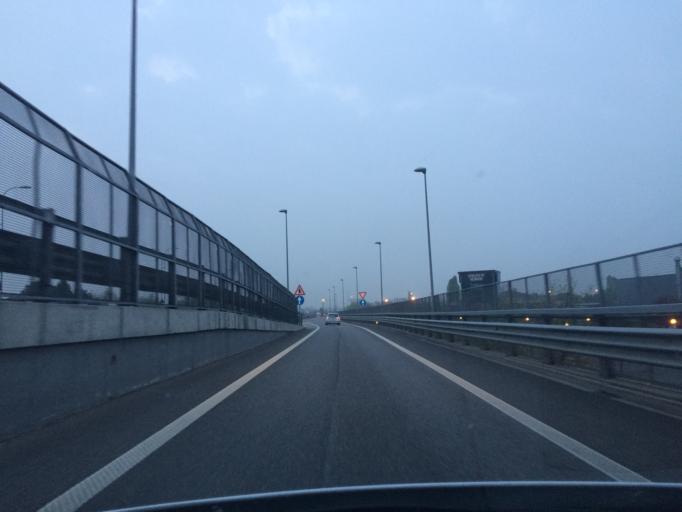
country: IT
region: Lombardy
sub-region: Provincia di Brescia
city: Roncadelle
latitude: 45.5246
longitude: 10.1773
